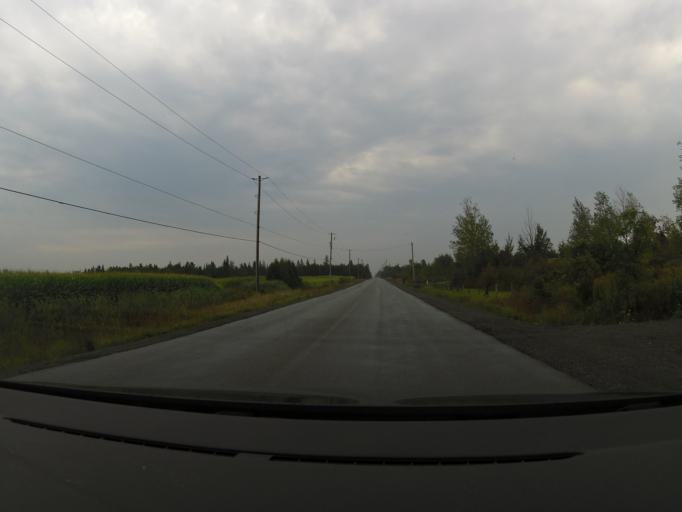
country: CA
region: Ontario
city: Carleton Place
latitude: 45.1932
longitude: -76.0723
